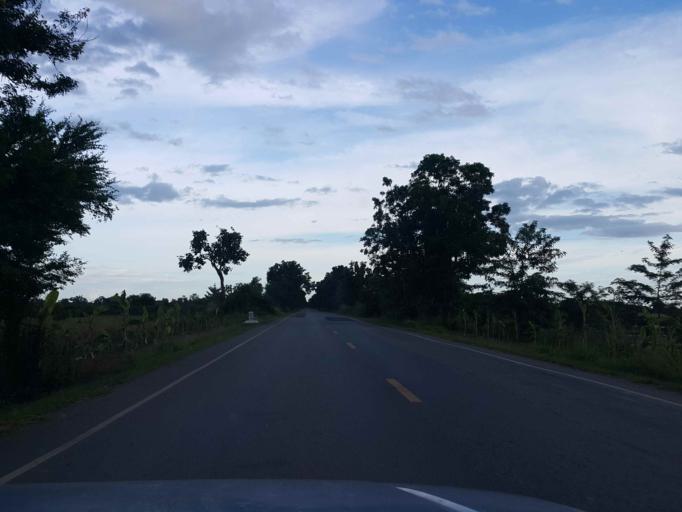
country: TH
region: Sukhothai
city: Sawankhalok
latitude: 17.3821
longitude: 99.7366
